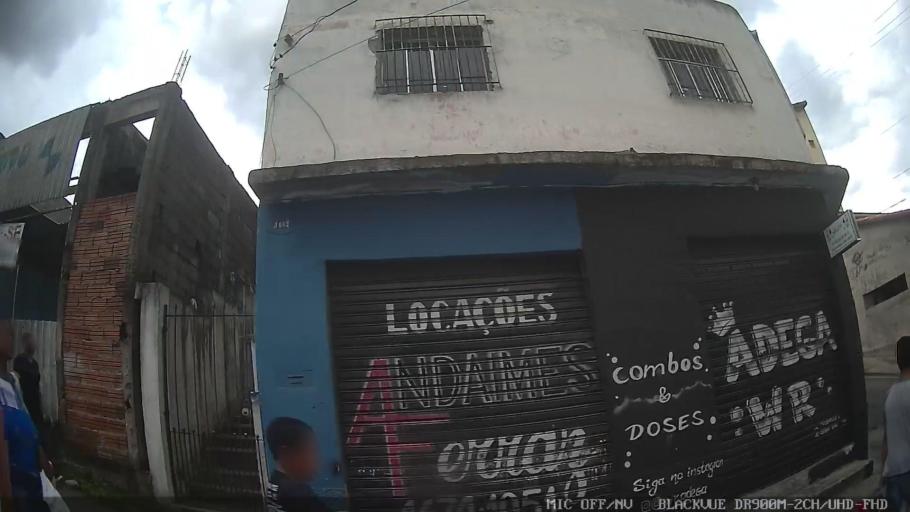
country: BR
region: Sao Paulo
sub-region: Ferraz De Vasconcelos
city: Ferraz de Vasconcelos
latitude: -23.5528
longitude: -46.3611
